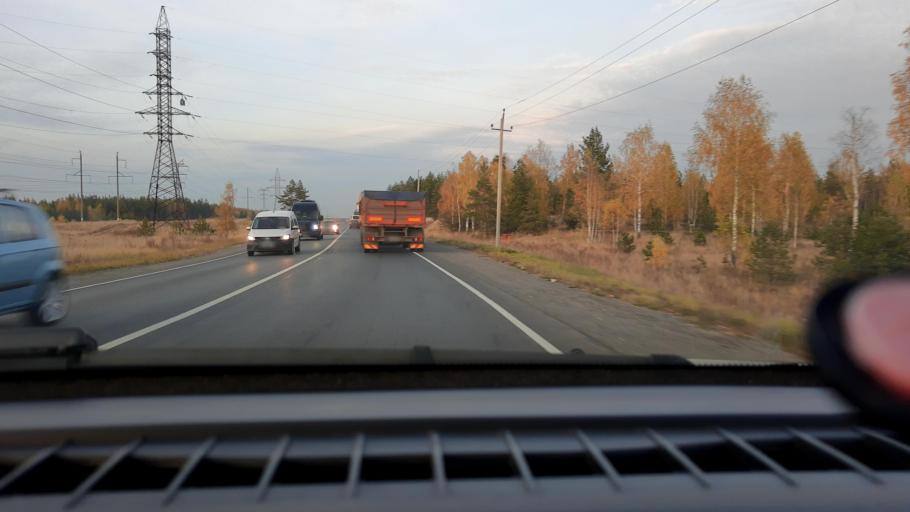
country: RU
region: Nizjnij Novgorod
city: Lukino
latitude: 56.3372
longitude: 43.5776
